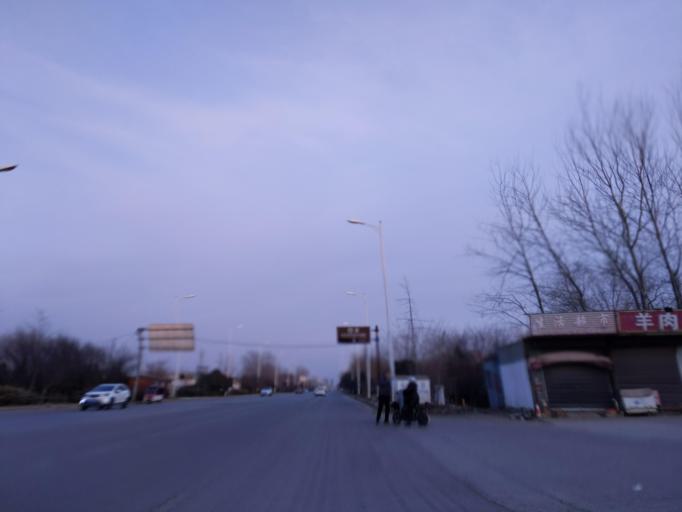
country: CN
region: Henan Sheng
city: Zhongyuanlu
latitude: 35.7872
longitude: 115.1188
